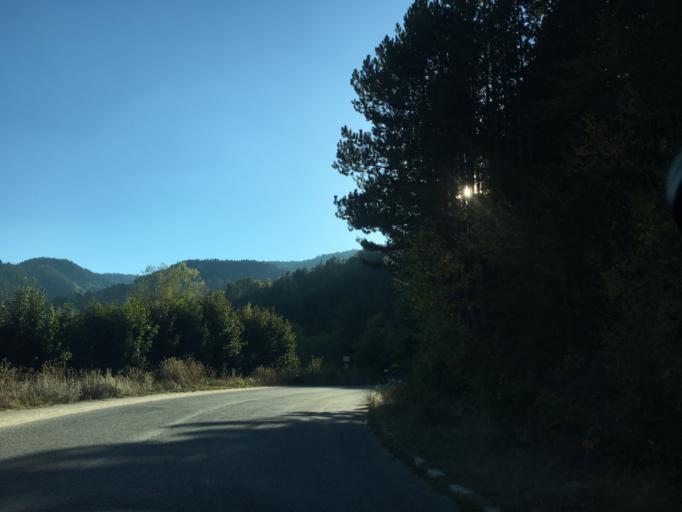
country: BG
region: Smolyan
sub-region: Obshtina Borino
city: Borino
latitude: 41.6051
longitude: 24.3810
